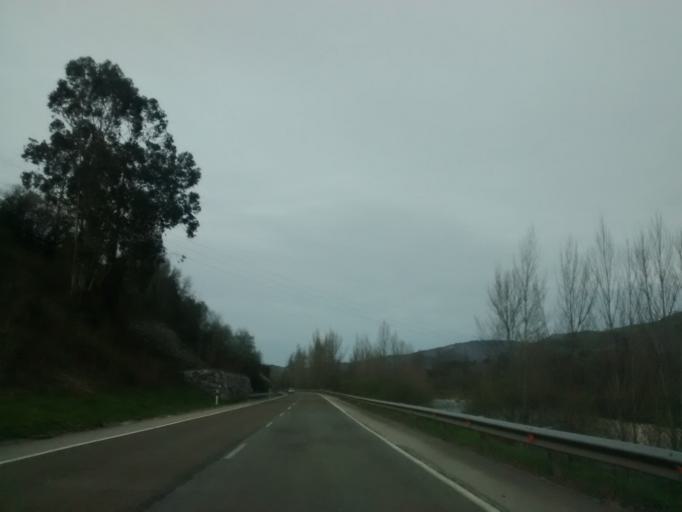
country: ES
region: Cantabria
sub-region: Provincia de Cantabria
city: Santiurde de Toranzo
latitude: 43.2291
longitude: -3.9464
